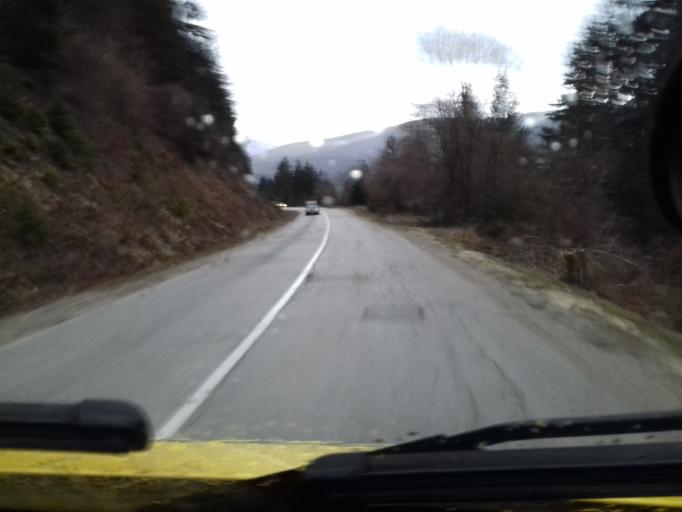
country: BA
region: Federation of Bosnia and Herzegovina
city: Turbe
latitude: 44.2815
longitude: 17.5081
